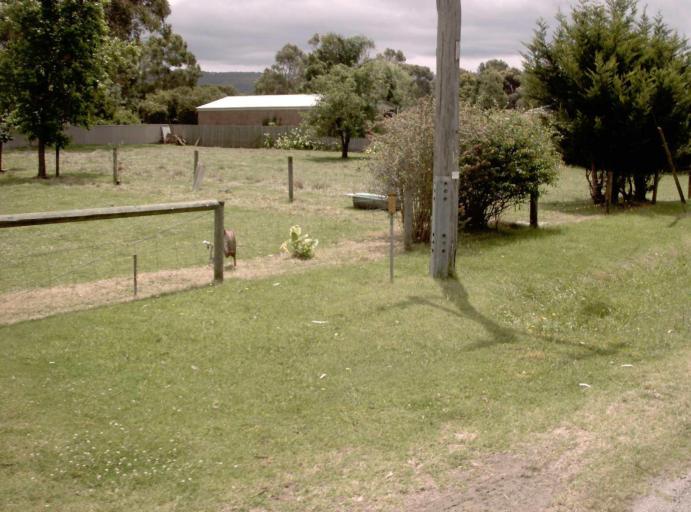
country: AU
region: Victoria
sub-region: Latrobe
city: Traralgon
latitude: -38.5288
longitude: 146.6591
